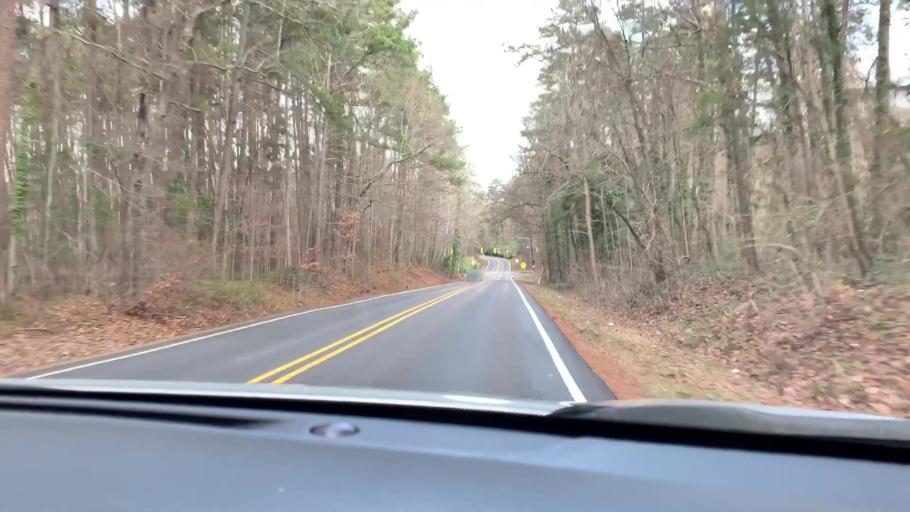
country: US
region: North Carolina
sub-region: Durham County
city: Durham
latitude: 35.9807
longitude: -78.9422
